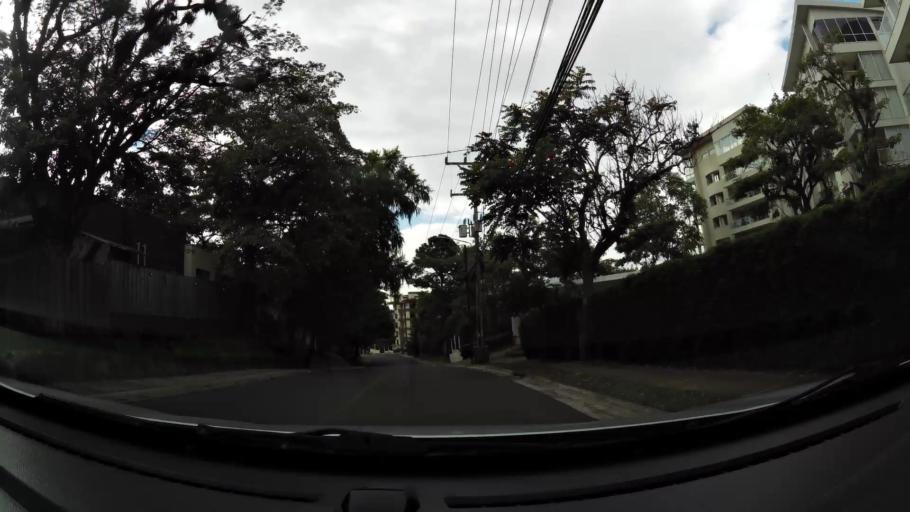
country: CR
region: San Jose
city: San Rafael
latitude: 9.9271
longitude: -84.1466
